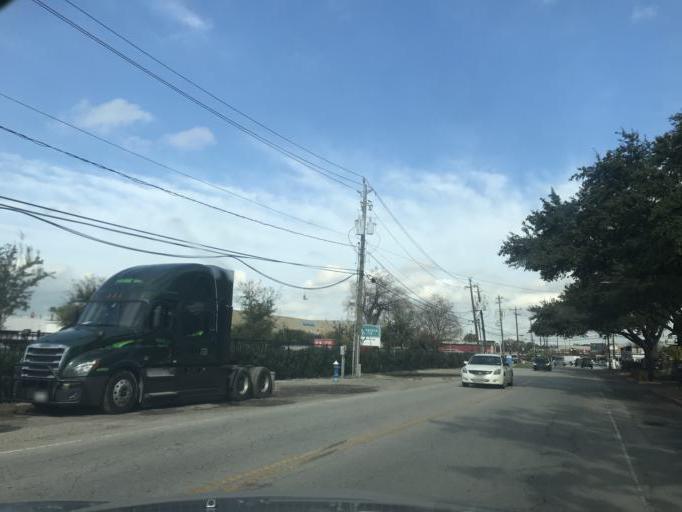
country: US
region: Texas
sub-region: Harris County
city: Hunters Creek Village
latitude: 29.7355
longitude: -95.4898
